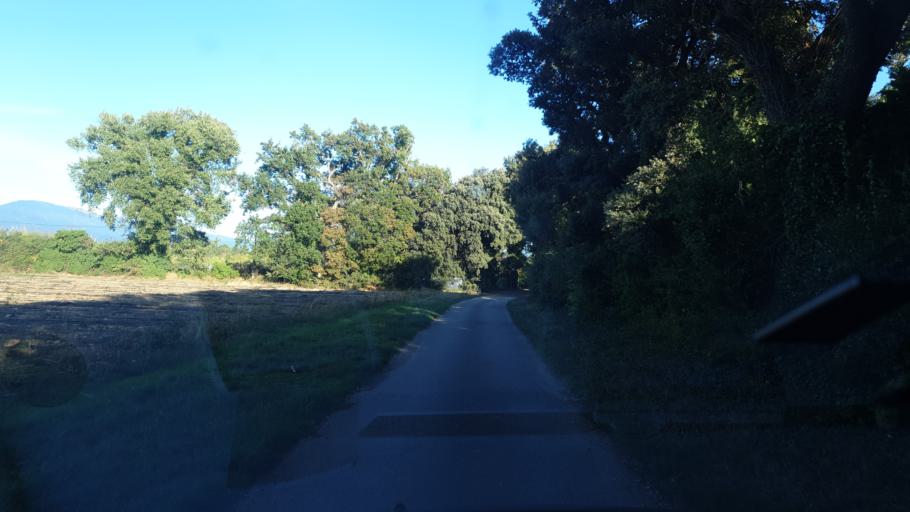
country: FR
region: Provence-Alpes-Cote d'Azur
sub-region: Departement du Vaucluse
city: Loriol-du-Comtat
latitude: 44.0589
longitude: 5.0144
